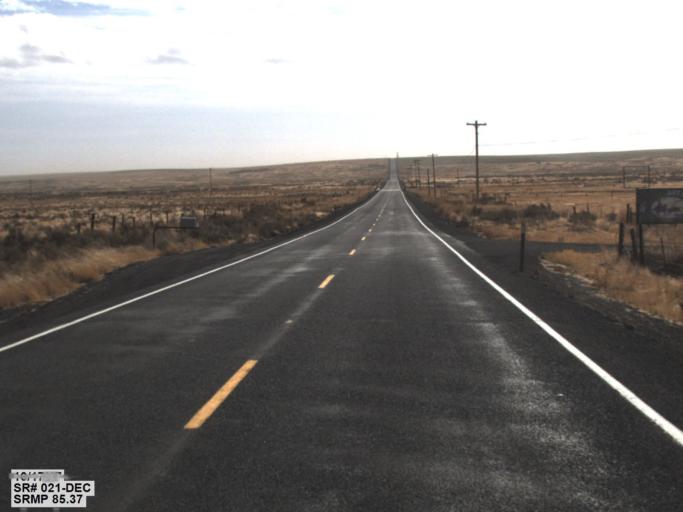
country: US
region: Washington
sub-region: Okanogan County
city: Coulee Dam
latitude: 47.6746
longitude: -118.7217
